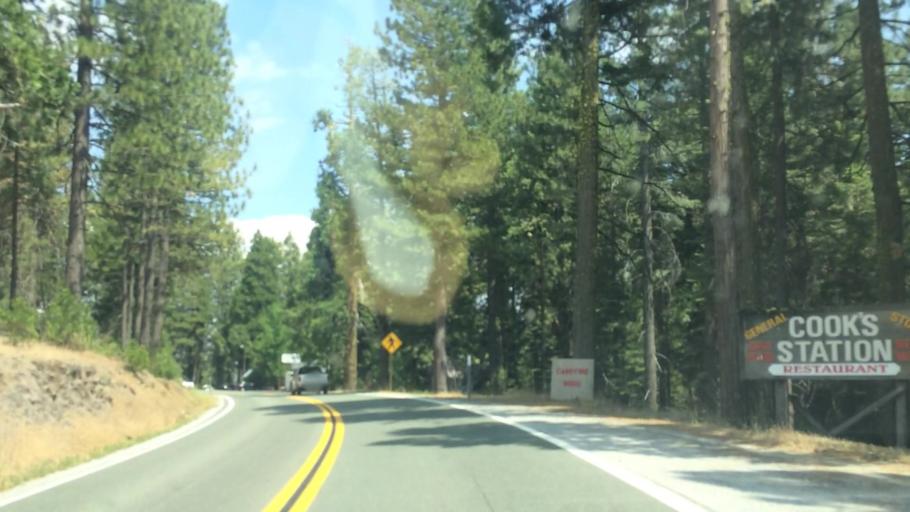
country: US
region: California
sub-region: Amador County
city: Pioneer
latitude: 38.5268
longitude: -120.4351
